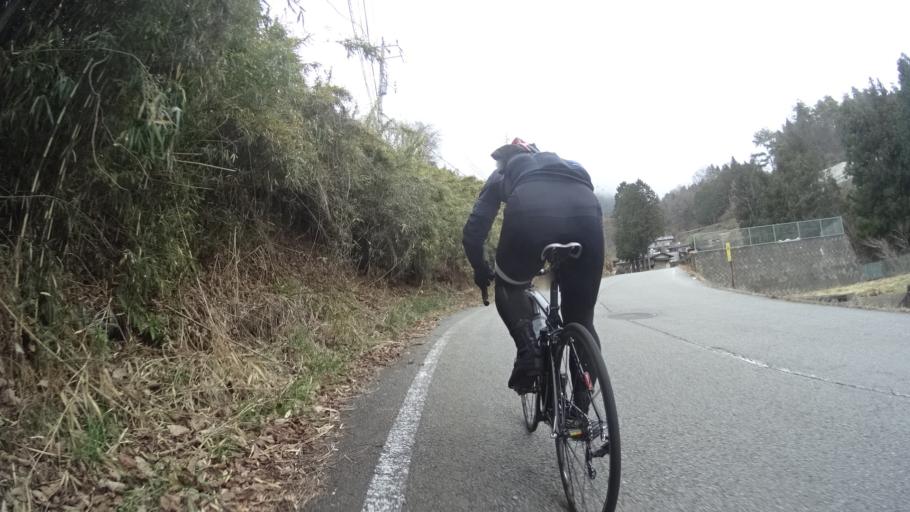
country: JP
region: Yamanashi
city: Otsuki
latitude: 35.6182
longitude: 139.0174
